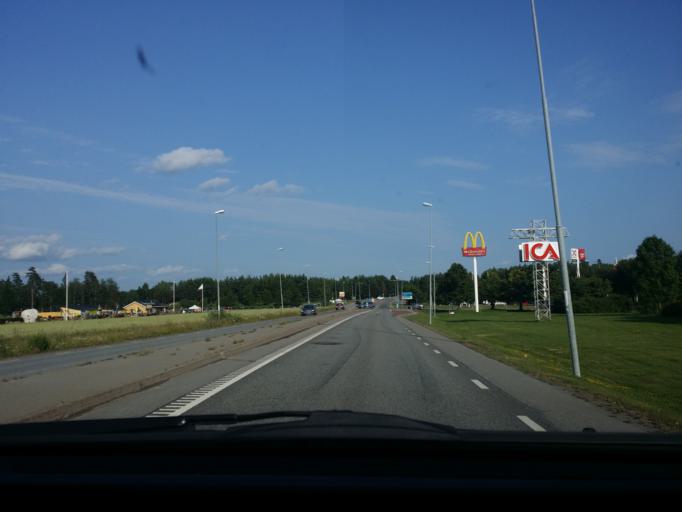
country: SE
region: Vaestmanland
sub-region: Vasteras
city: Hokasen
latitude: 59.6107
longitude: 16.6225
